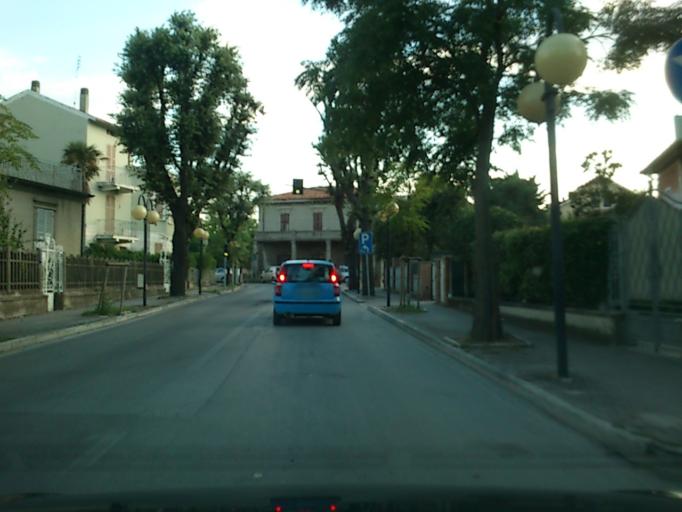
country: IT
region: The Marches
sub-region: Provincia di Pesaro e Urbino
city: Fano
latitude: 43.8493
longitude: 13.0099
